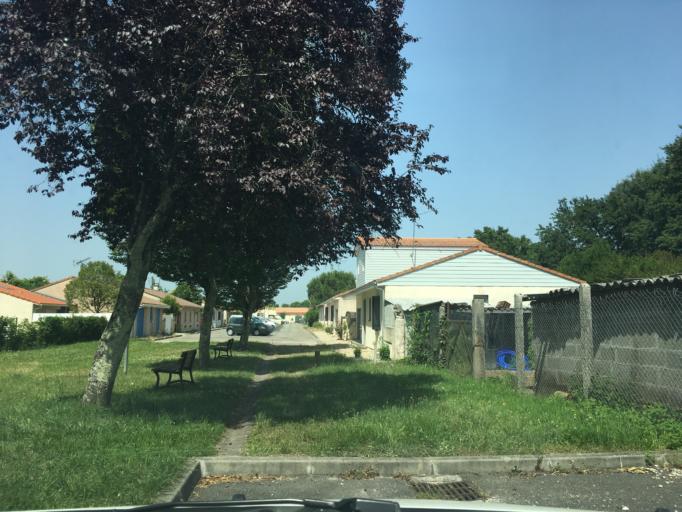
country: FR
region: Aquitaine
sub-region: Departement de la Gironde
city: Cantenac
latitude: 45.0235
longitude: -0.6358
